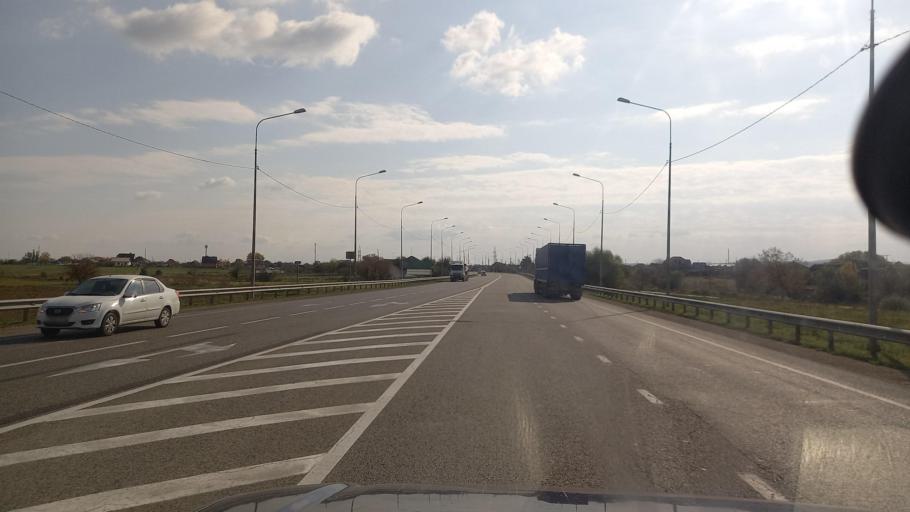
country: RU
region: Krasnodarskiy
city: Novoukrainskiy
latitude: 44.9000
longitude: 38.0392
